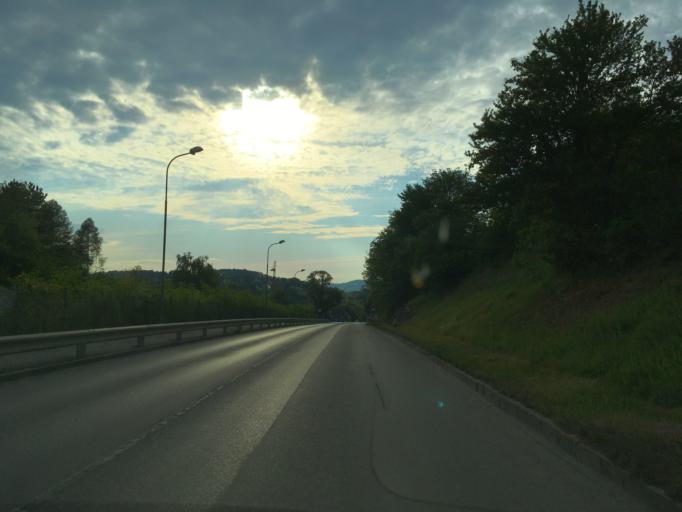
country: AT
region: Lower Austria
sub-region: Politischer Bezirk Sankt Polten
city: Neulengbach
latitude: 48.1959
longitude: 15.9091
